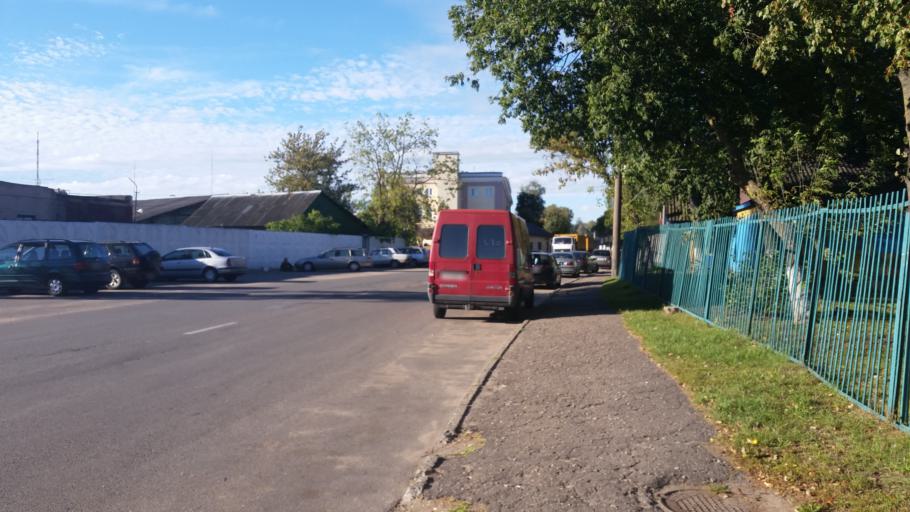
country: BY
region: Vitebsk
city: Vitebsk
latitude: 55.1792
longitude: 30.1874
